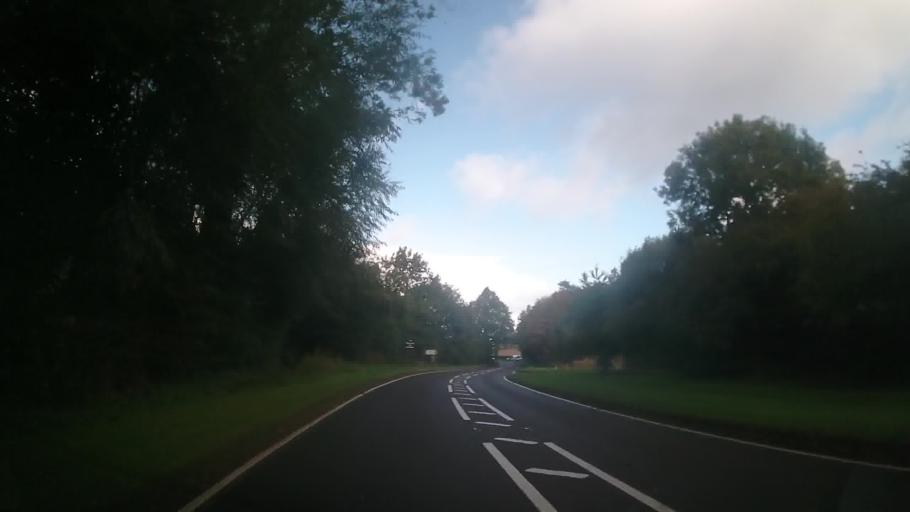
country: GB
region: England
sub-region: Gloucestershire
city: Moreton in Marsh
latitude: 51.9690
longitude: -1.6276
